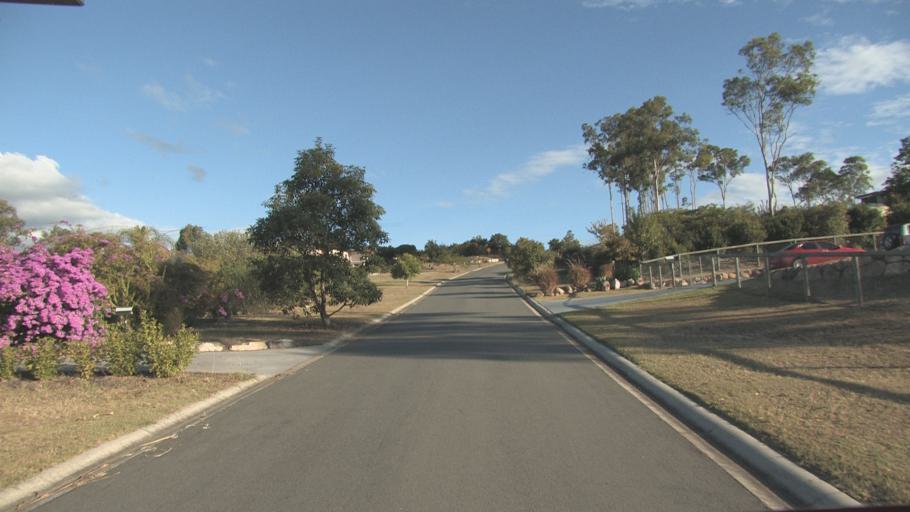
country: AU
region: Queensland
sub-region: Logan
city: Cedar Vale
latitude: -27.8644
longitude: 153.0839
